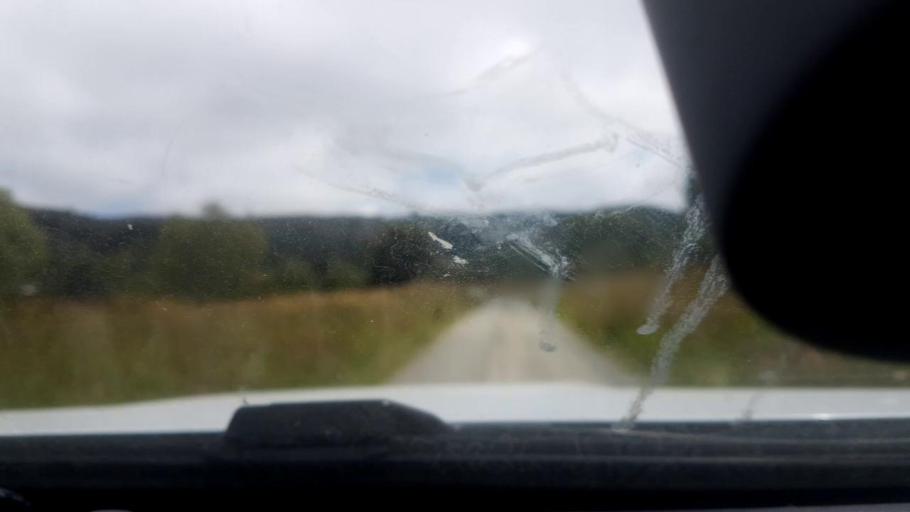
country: NZ
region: Canterbury
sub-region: Timaru District
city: Pleasant Point
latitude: -44.1388
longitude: 171.0835
